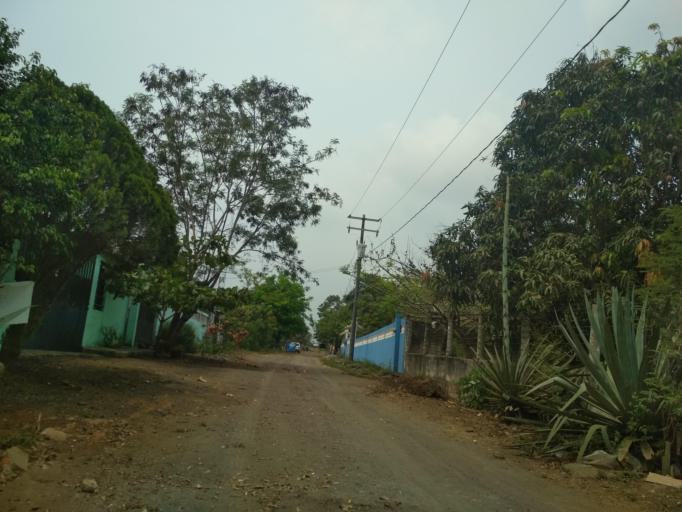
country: MX
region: Veracruz
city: Paso del Toro
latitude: 19.0233
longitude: -96.1372
